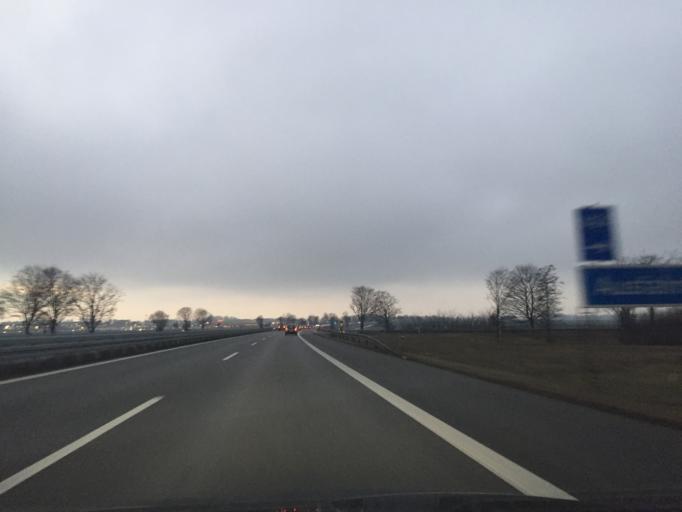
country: DE
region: Bavaria
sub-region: Upper Bavaria
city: Schwifting
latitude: 48.0573
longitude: 10.9060
